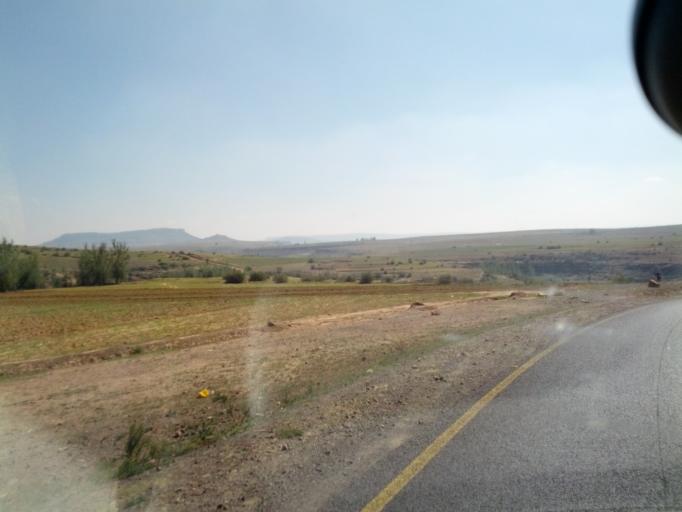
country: LS
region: Berea
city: Teyateyaneng
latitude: -29.1384
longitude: 27.7042
